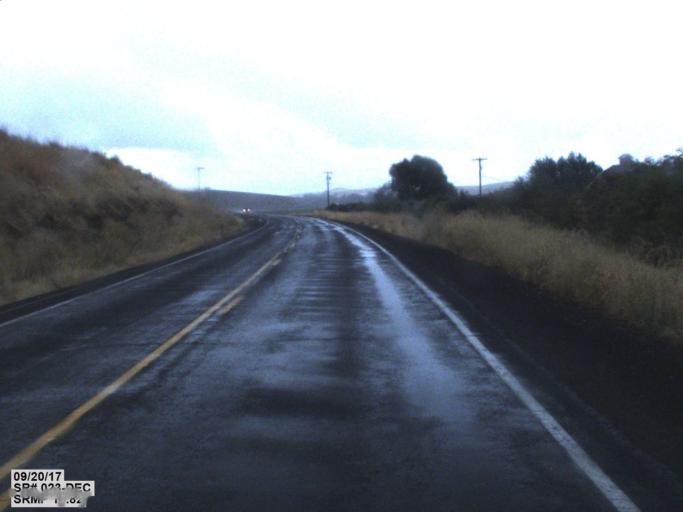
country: US
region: Washington
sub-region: Whitman County
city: Colfax
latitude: 47.1015
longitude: -117.6126
